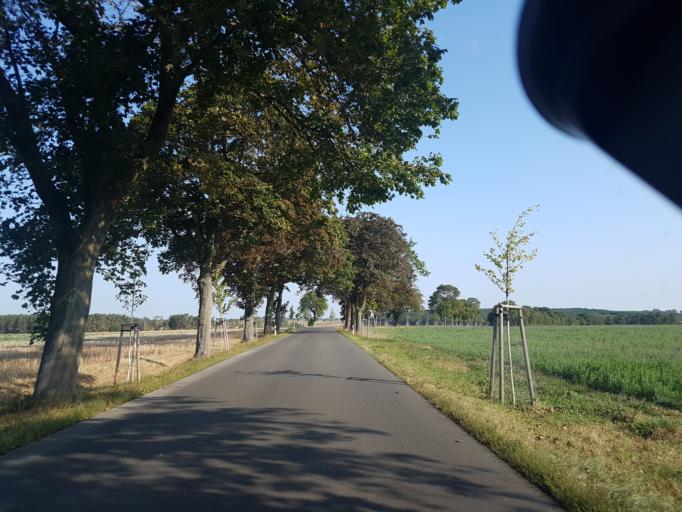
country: DE
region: Saxony-Anhalt
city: Kropstadt
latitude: 51.9965
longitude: 12.6800
